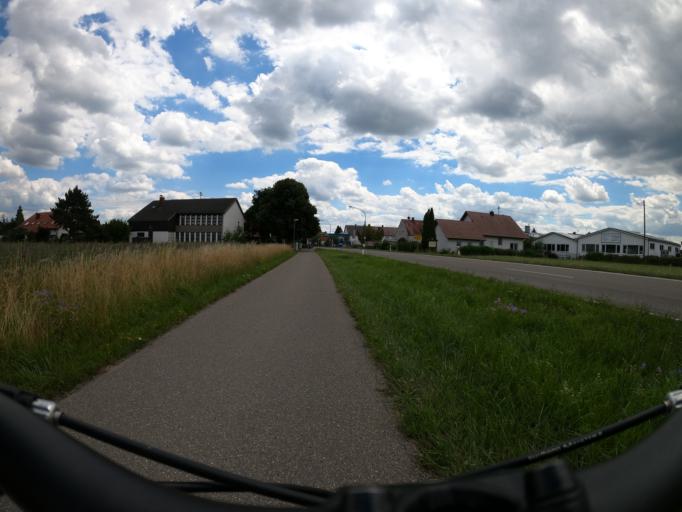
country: DE
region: Bavaria
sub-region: Swabia
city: Nersingen
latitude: 48.4195
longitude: 10.1324
